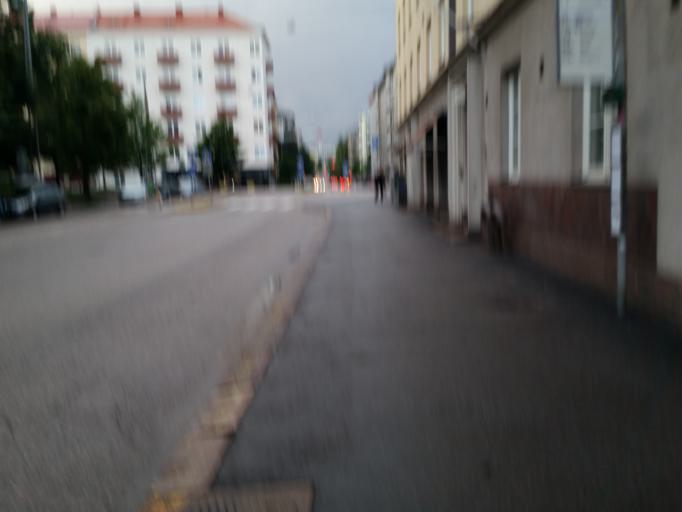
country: FI
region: Uusimaa
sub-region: Helsinki
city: Helsinki
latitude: 60.1832
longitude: 24.9186
